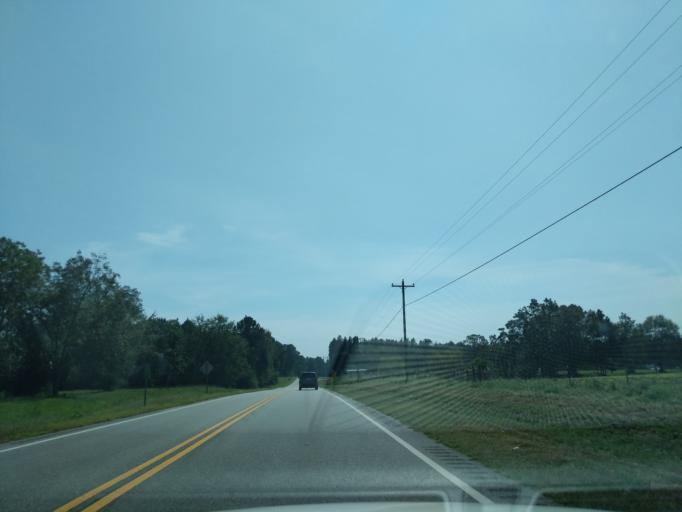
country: US
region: Alabama
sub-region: Covington County
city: Andalusia
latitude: 31.2330
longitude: -86.5278
